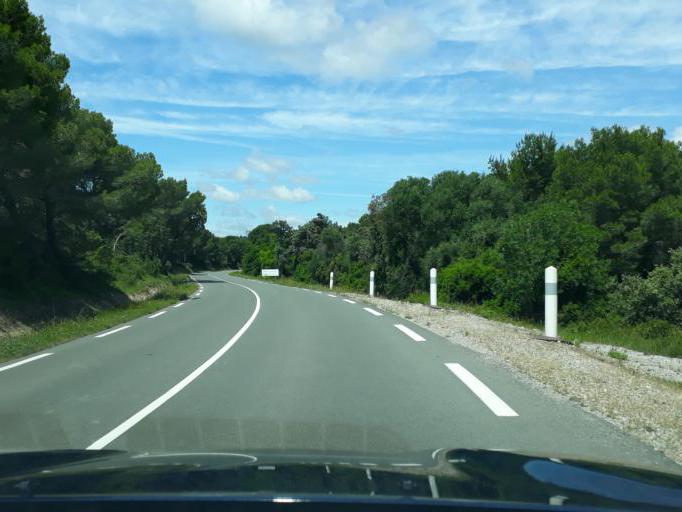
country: FR
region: Languedoc-Roussillon
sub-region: Departement de l'Aude
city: Sigean
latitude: 43.0387
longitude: 2.9489
